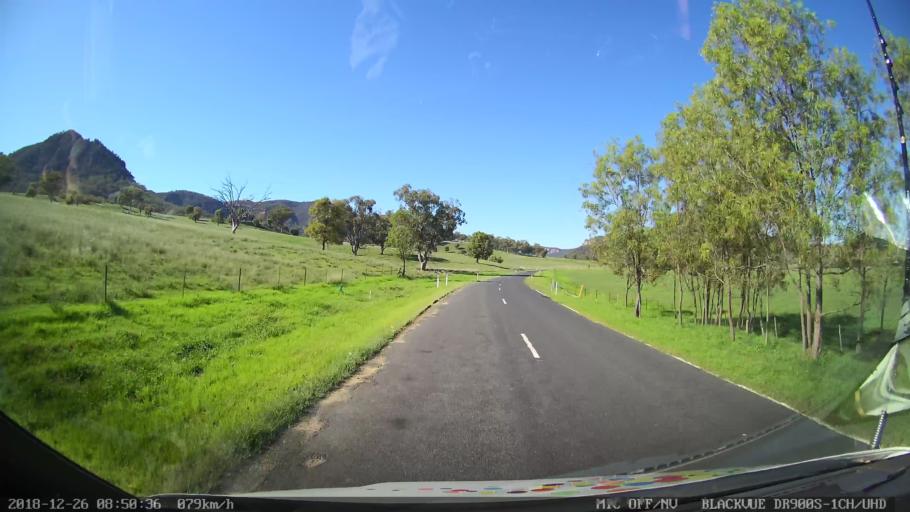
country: AU
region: New South Wales
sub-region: Mid-Western Regional
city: Kandos
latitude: -32.5773
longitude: 150.0944
